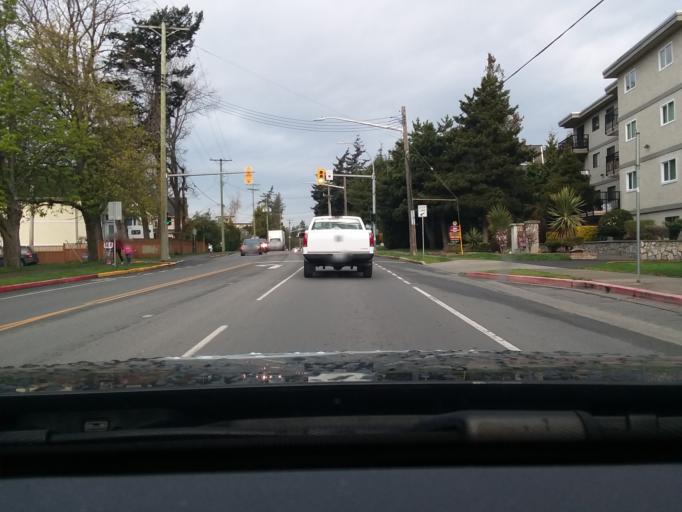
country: CA
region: British Columbia
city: Victoria
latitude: 48.4402
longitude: -123.3953
